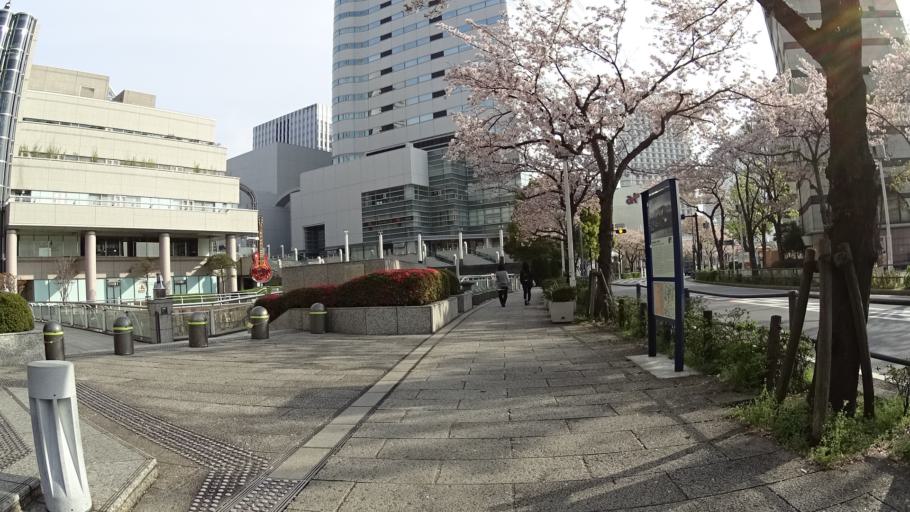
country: JP
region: Kanagawa
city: Yokohama
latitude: 35.4548
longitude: 139.6325
